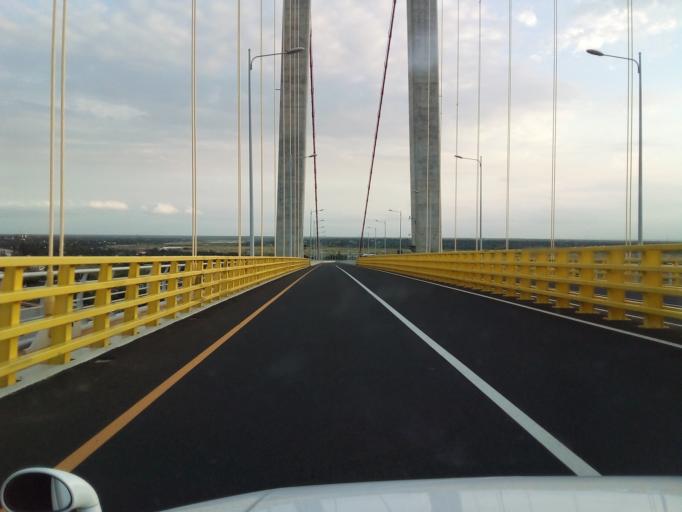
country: MZ
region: Maputo City
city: Maputo
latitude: -25.9740
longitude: 32.5569
